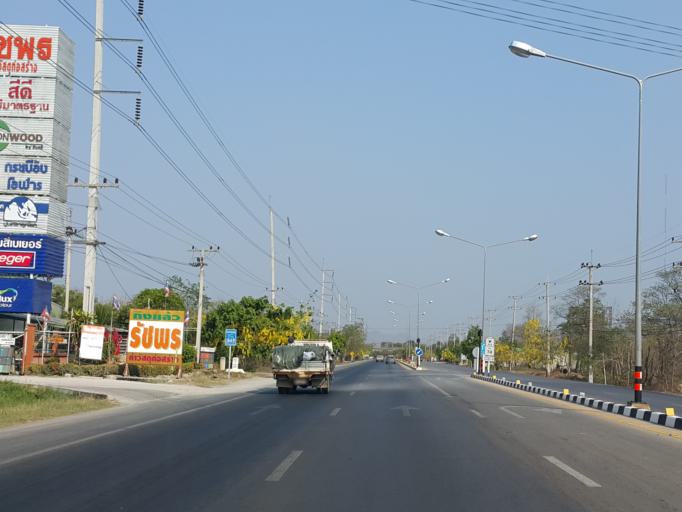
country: TH
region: Kanchanaburi
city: Kanchanaburi
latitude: 14.0640
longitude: 99.4169
